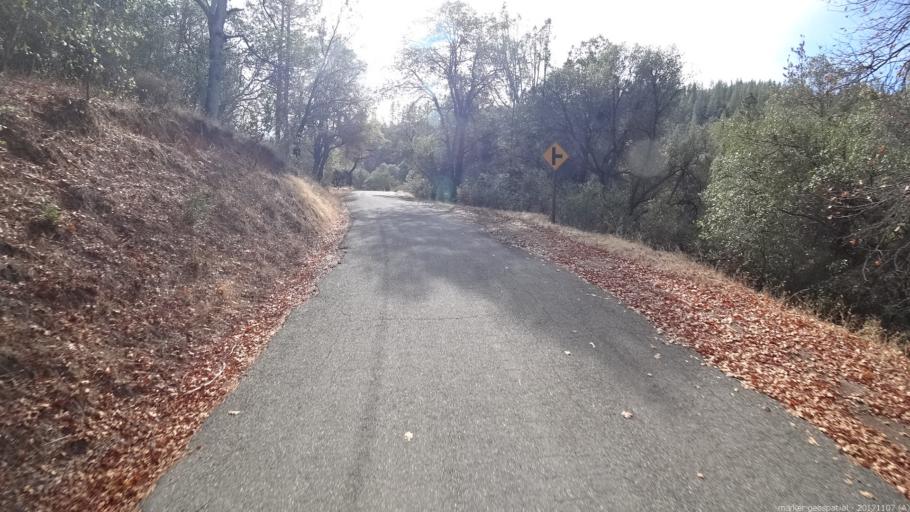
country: US
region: California
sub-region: Shasta County
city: Shasta
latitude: 40.5397
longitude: -122.5669
